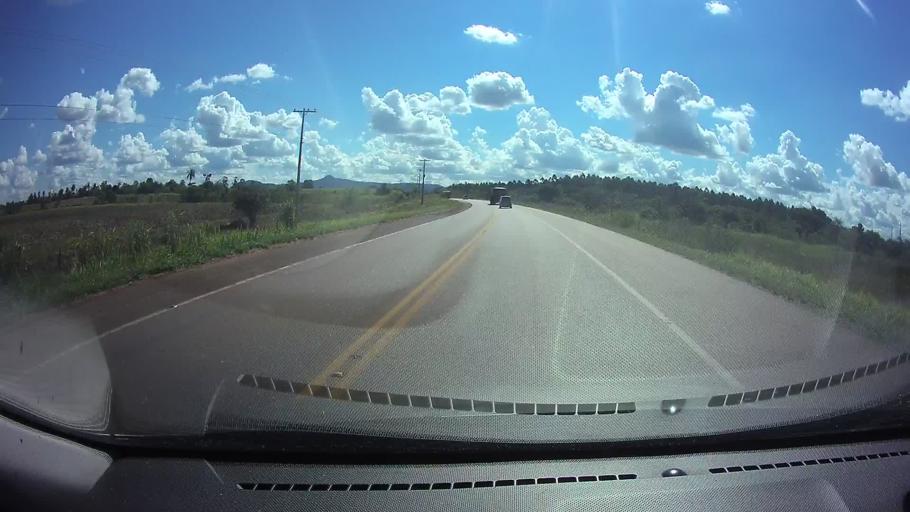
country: PY
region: Guaira
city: Coronel Martinez
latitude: -25.7585
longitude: -56.7059
